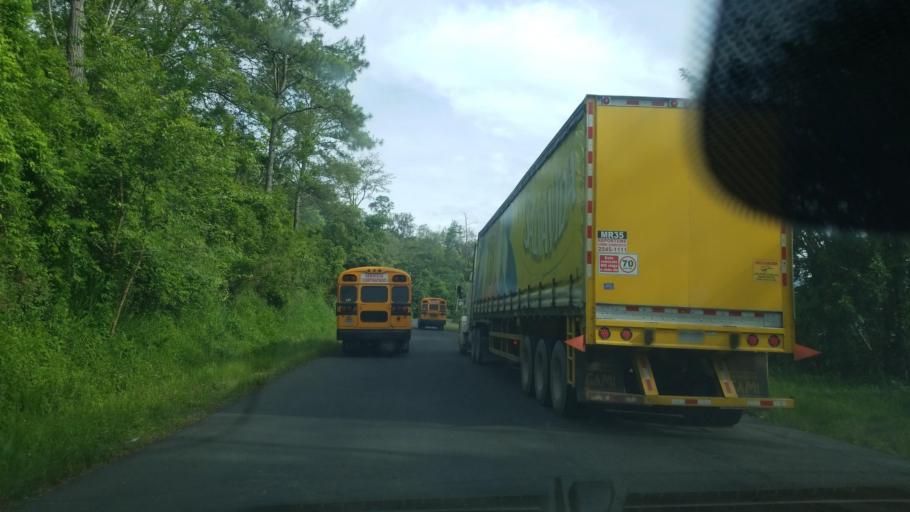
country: HN
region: Santa Barbara
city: Petoa
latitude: 15.2053
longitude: -88.2697
